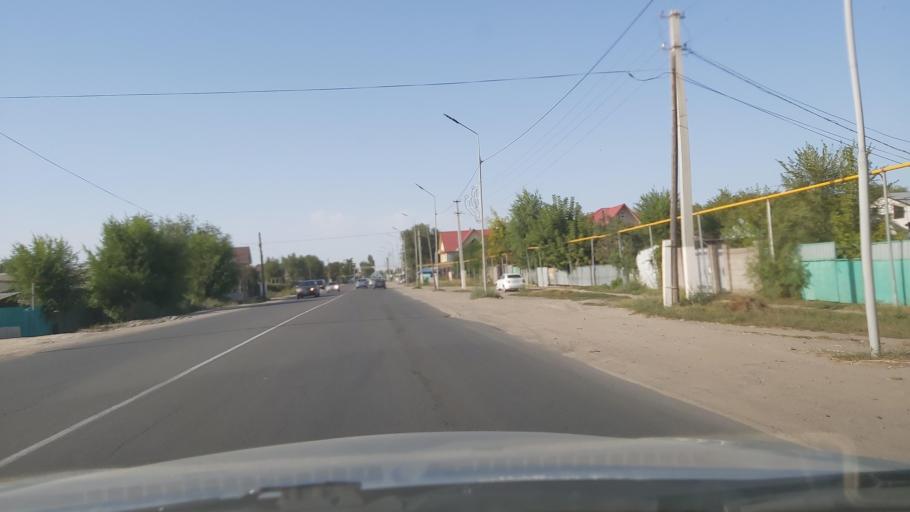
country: KZ
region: Almaty Oblysy
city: Energeticheskiy
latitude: 43.4874
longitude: 77.0341
